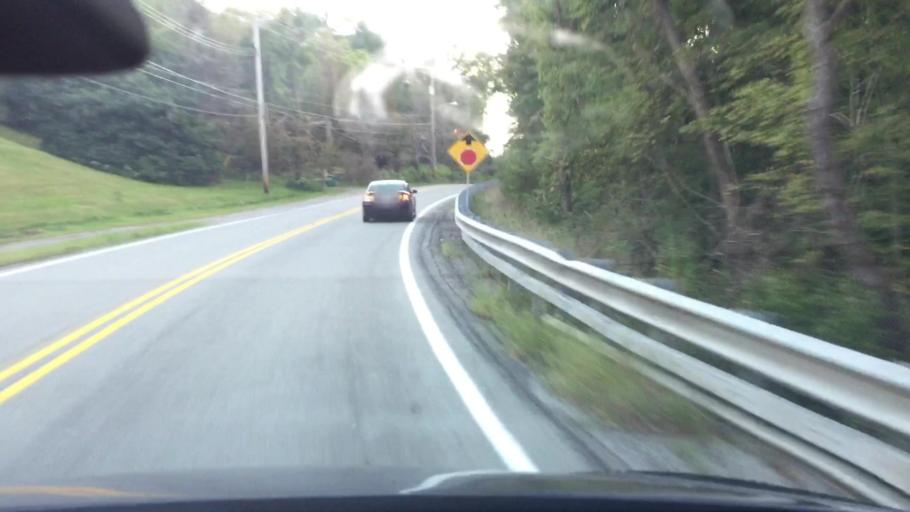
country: US
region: Pennsylvania
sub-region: Allegheny County
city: Allison Park
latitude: 40.5445
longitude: -79.9188
